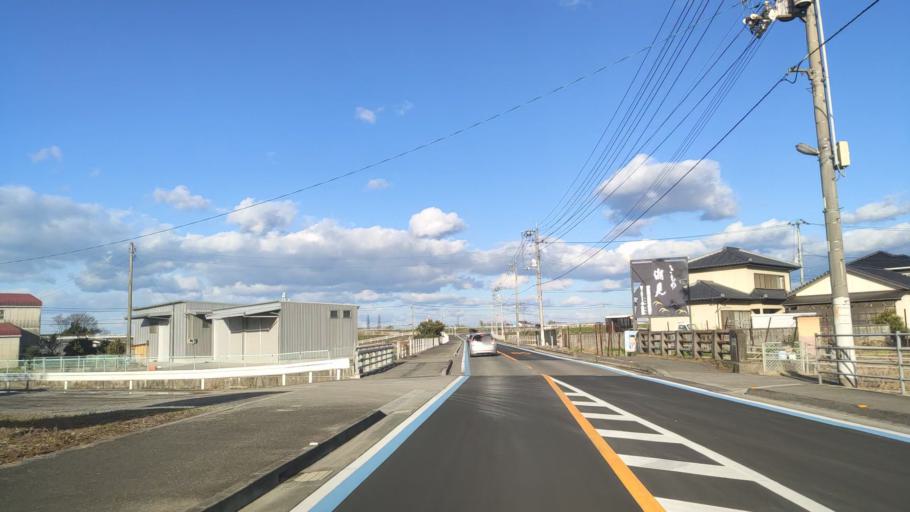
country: JP
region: Ehime
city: Saijo
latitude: 33.9093
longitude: 133.1573
